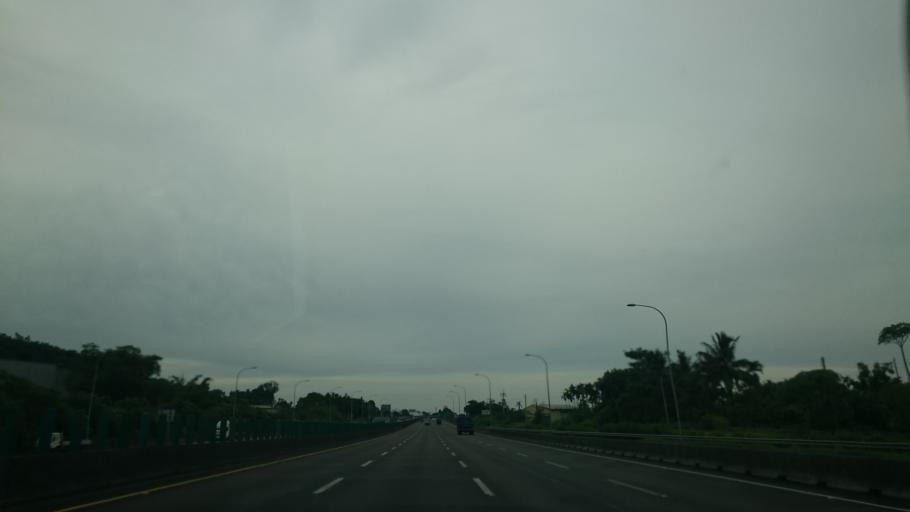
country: TW
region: Taiwan
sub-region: Nantou
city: Nantou
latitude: 23.8730
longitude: 120.7060
